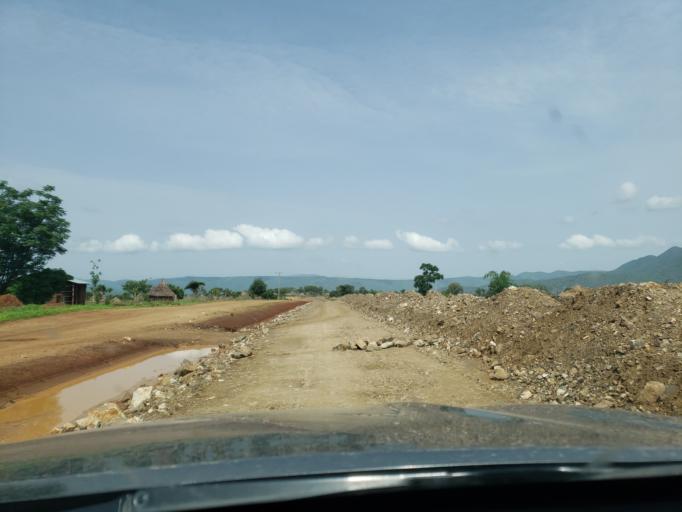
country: ET
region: Oromiya
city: Mendi
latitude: 10.1211
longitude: 35.1486
